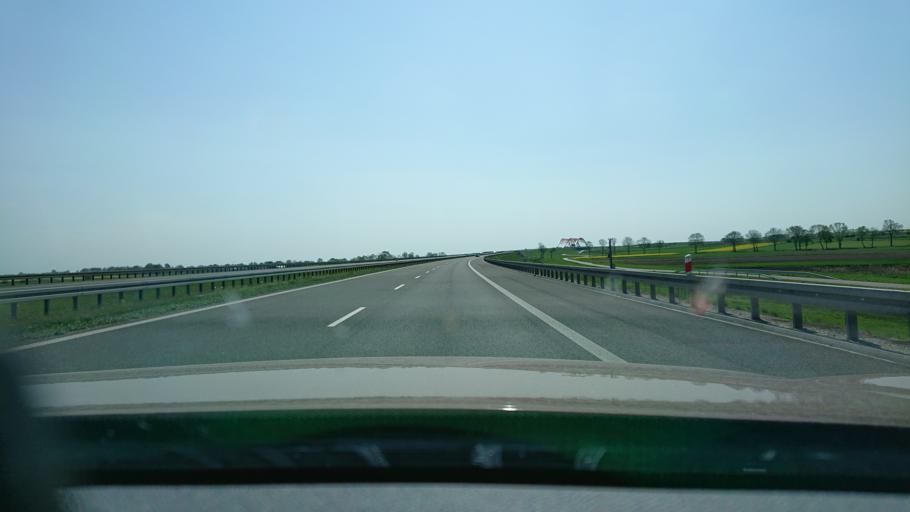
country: PL
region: Subcarpathian Voivodeship
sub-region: Powiat przeworski
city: Rozborz
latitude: 50.0715
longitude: 22.5523
